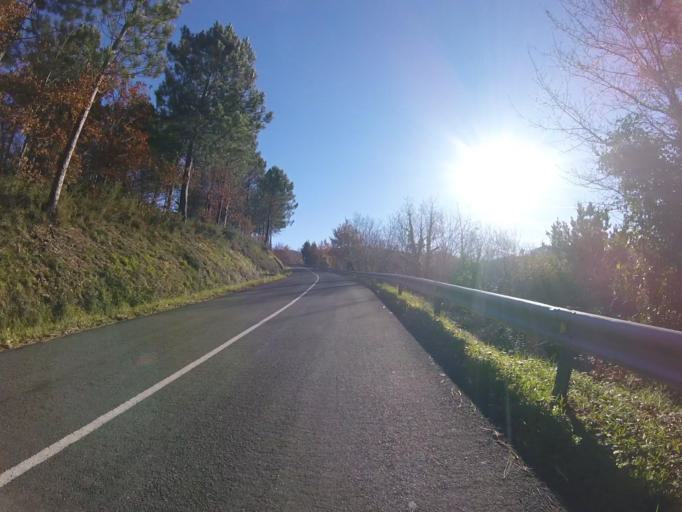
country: ES
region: Basque Country
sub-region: Provincia de Guipuzcoa
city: Irun
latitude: 43.3189
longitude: -1.7689
